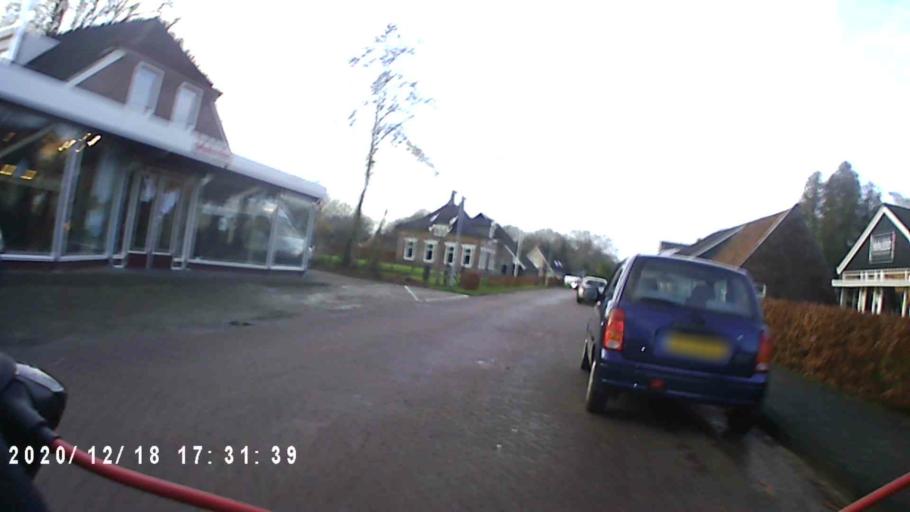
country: NL
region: Drenthe
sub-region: Gemeente Tynaarlo
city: Vries
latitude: 53.0789
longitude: 6.5764
